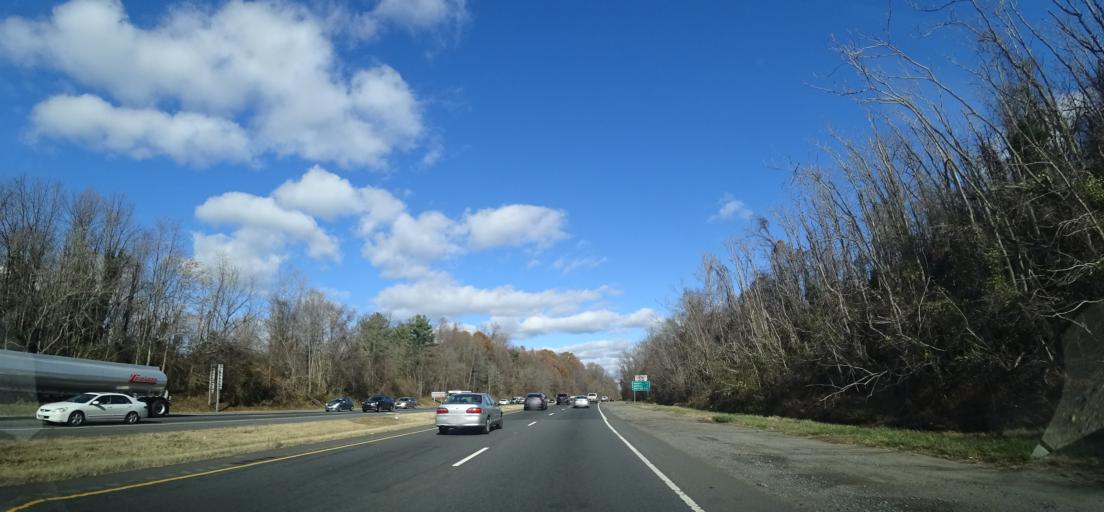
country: US
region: Virginia
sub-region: Fauquier County
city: Warrenton
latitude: 38.6866
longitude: -77.7870
